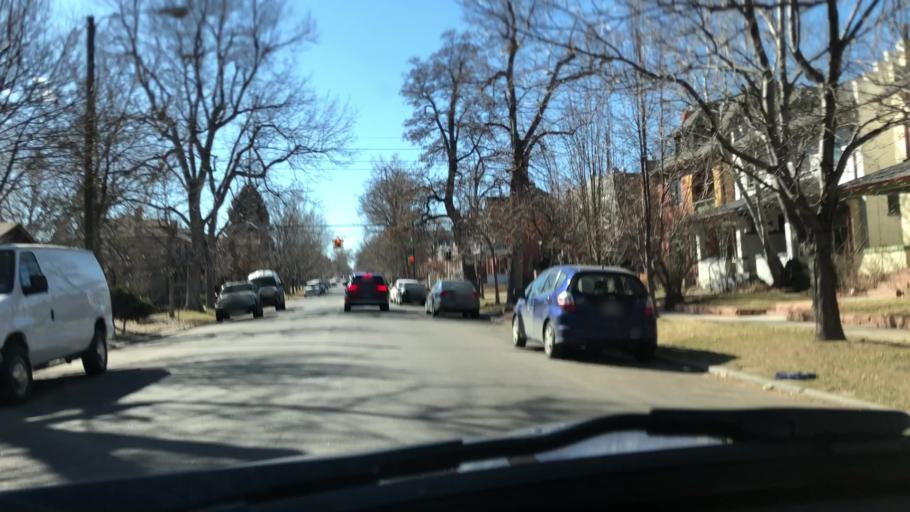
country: US
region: Colorado
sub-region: Denver County
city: Denver
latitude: 39.7515
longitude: -104.9647
